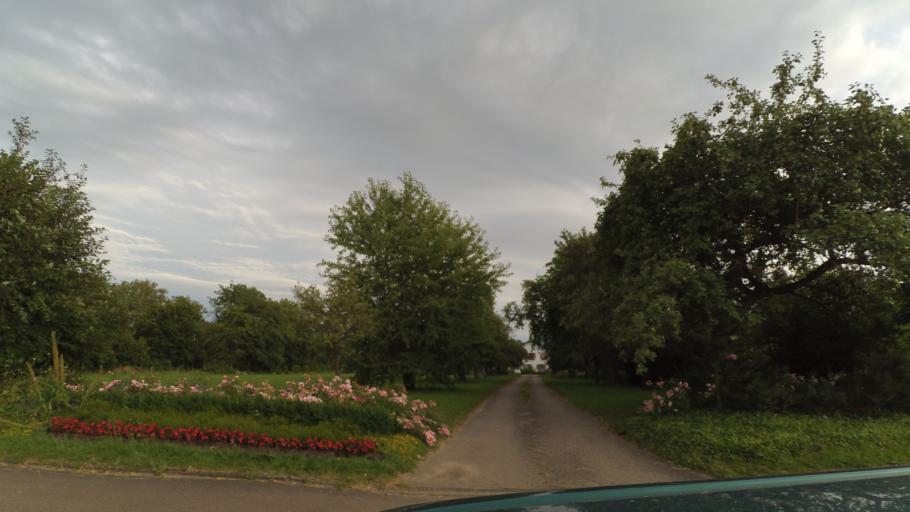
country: DE
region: Bavaria
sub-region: Swabia
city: Hochstadt an der Donau
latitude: 48.6232
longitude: 10.5925
